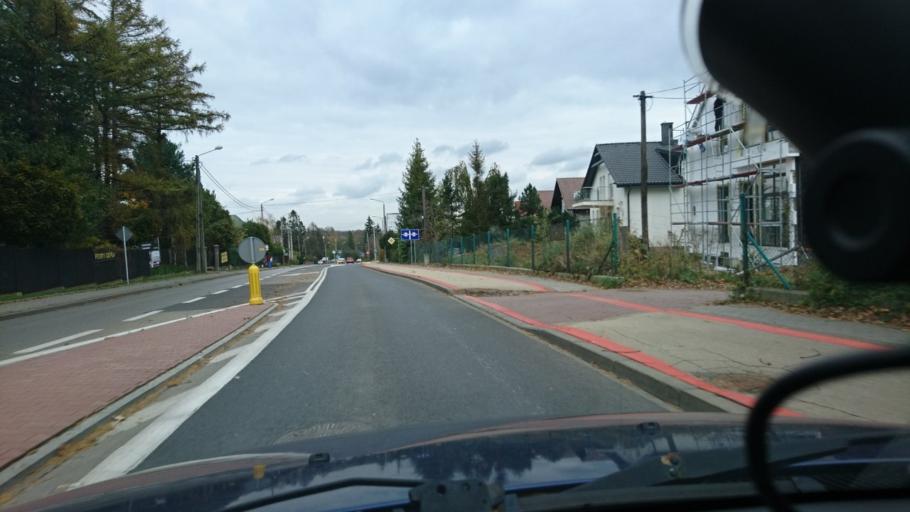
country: PL
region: Silesian Voivodeship
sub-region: Bielsko-Biala
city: Bielsko-Biala
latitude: 49.7954
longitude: 19.0390
